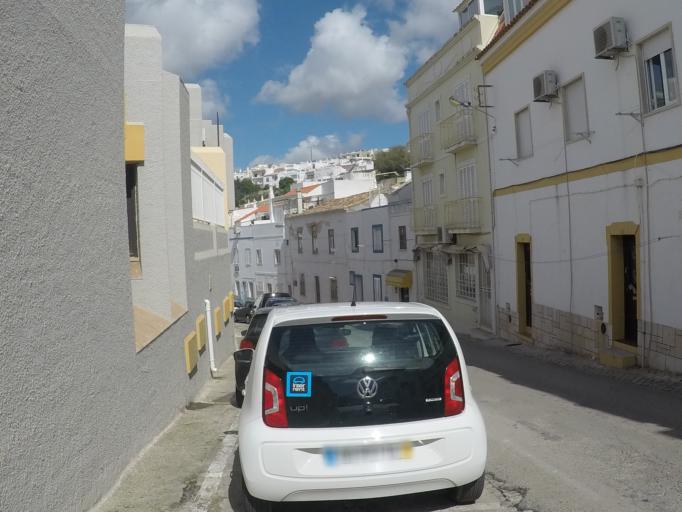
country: PT
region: Faro
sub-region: Albufeira
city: Albufeira
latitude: 37.0991
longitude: -8.2392
